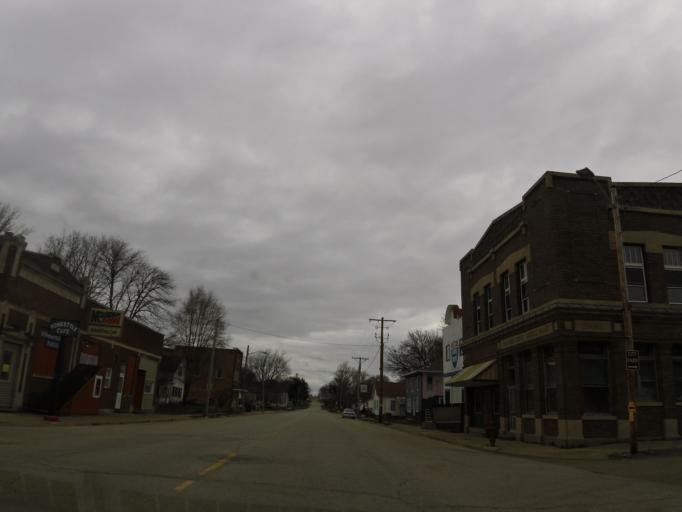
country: US
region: Iowa
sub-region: Benton County
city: Vinton
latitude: 42.3144
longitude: -92.0019
